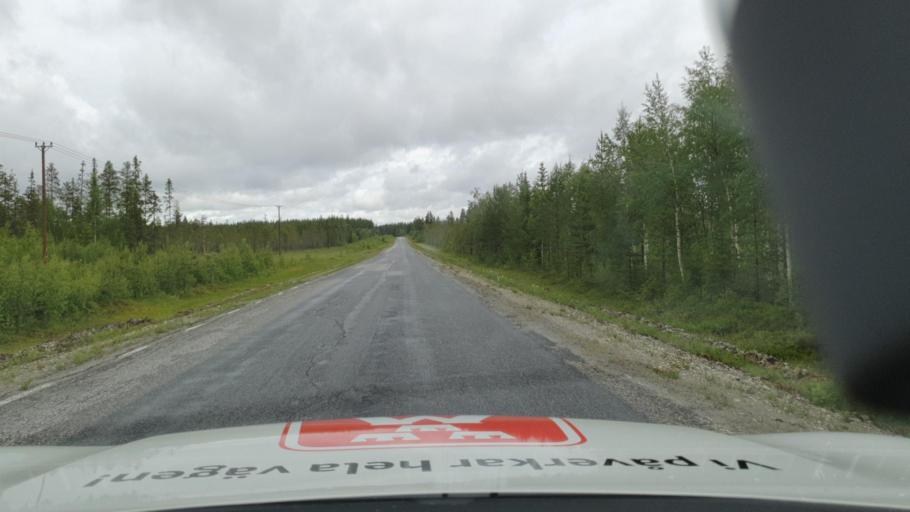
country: SE
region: Vaesterbotten
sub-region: Dorotea Kommun
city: Dorotea
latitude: 64.1322
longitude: 16.6358
